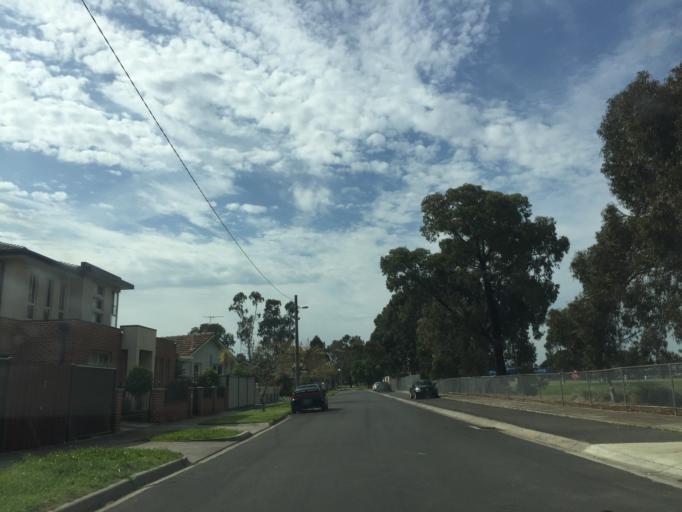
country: AU
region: Victoria
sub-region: Darebin
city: Preston
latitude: -37.7496
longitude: 145.0188
